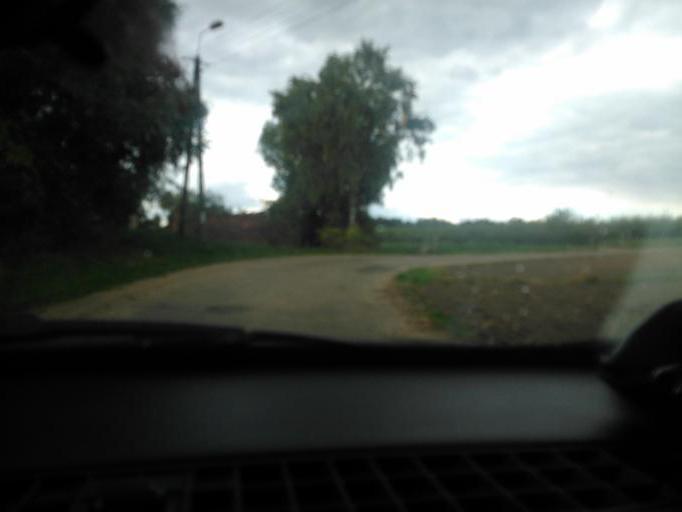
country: PL
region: Kujawsko-Pomorskie
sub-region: Powiat brodnicki
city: Swiedziebnia
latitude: 53.2185
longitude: 19.5225
